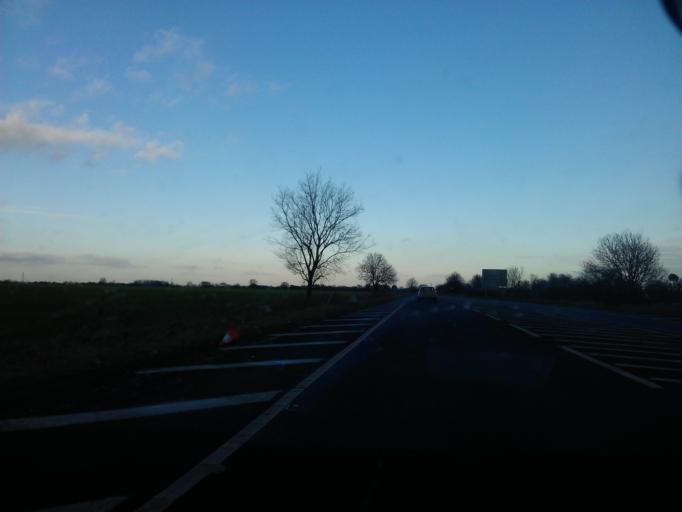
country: GB
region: England
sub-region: Essex
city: Great Bentley
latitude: 51.8899
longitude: 1.0627
